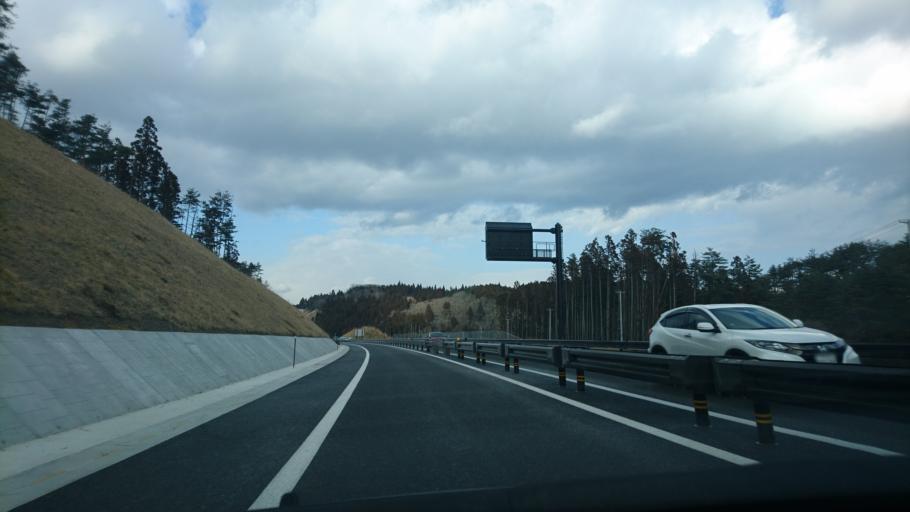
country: JP
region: Miyagi
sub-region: Oshika Gun
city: Onagawa Cho
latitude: 38.7125
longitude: 141.5096
